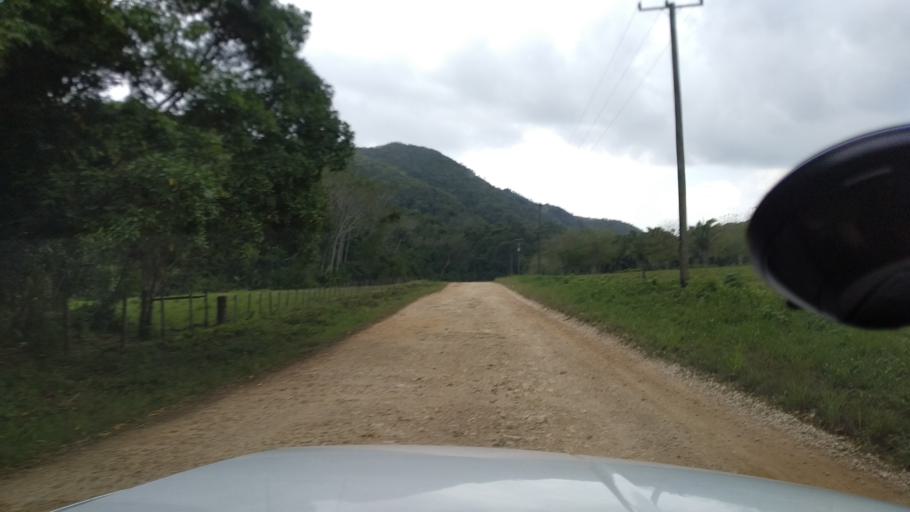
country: BZ
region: Toledo
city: Punta Gorda
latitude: 16.2093
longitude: -89.0240
